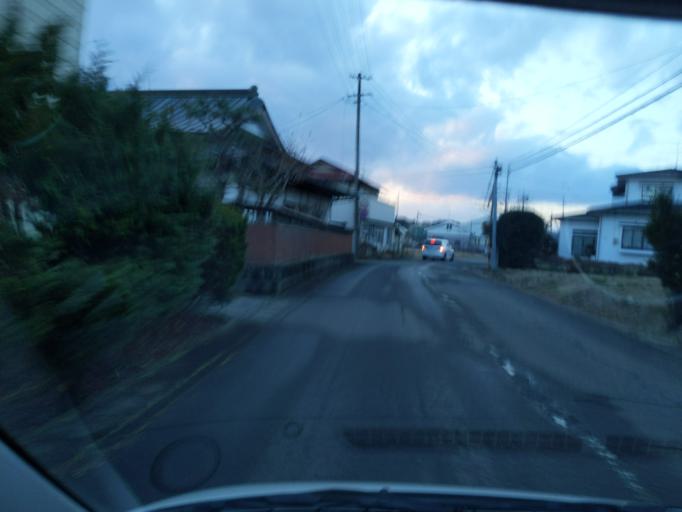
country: JP
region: Iwate
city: Ichinoseki
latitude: 38.8027
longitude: 141.1170
